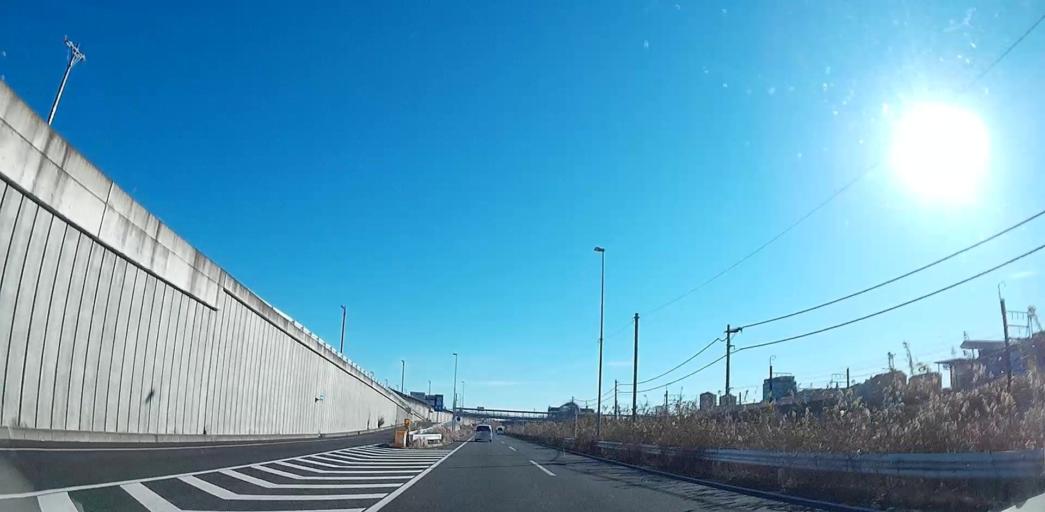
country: JP
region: Chiba
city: Shiroi
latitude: 35.8048
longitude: 140.1631
